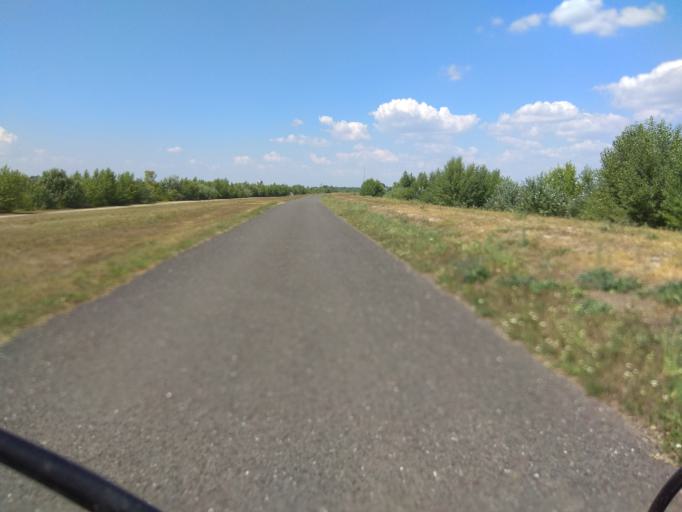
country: SK
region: Trnavsky
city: Gabcikovo
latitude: 47.8658
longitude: 17.5593
